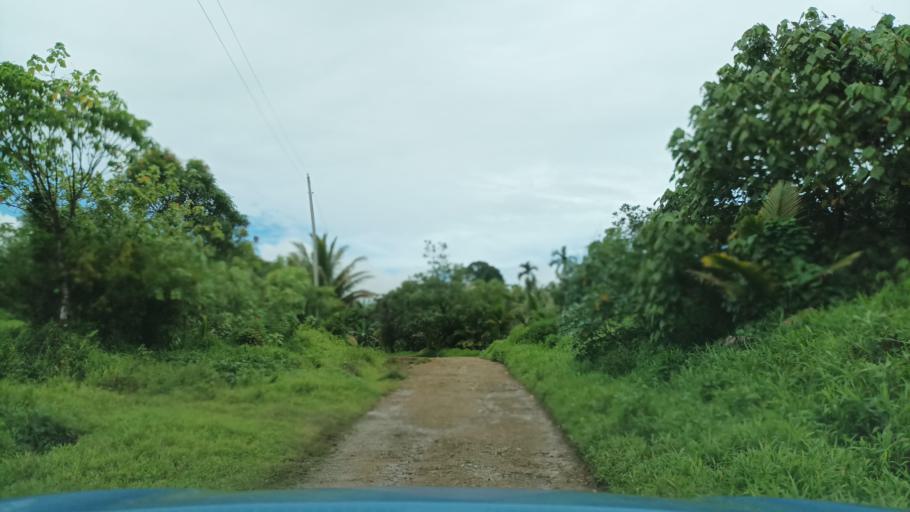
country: FM
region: Pohnpei
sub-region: Sokehs Municipality
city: Palikir - National Government Center
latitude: 6.8521
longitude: 158.1829
